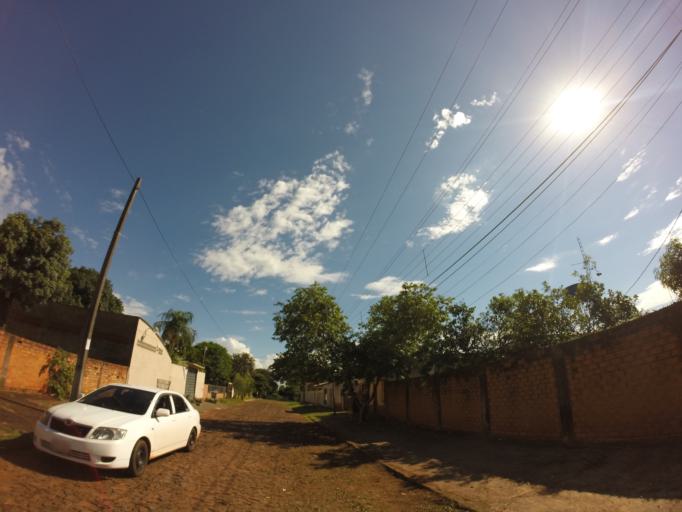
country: PY
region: Alto Parana
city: Ciudad del Este
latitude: -25.4067
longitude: -54.6251
